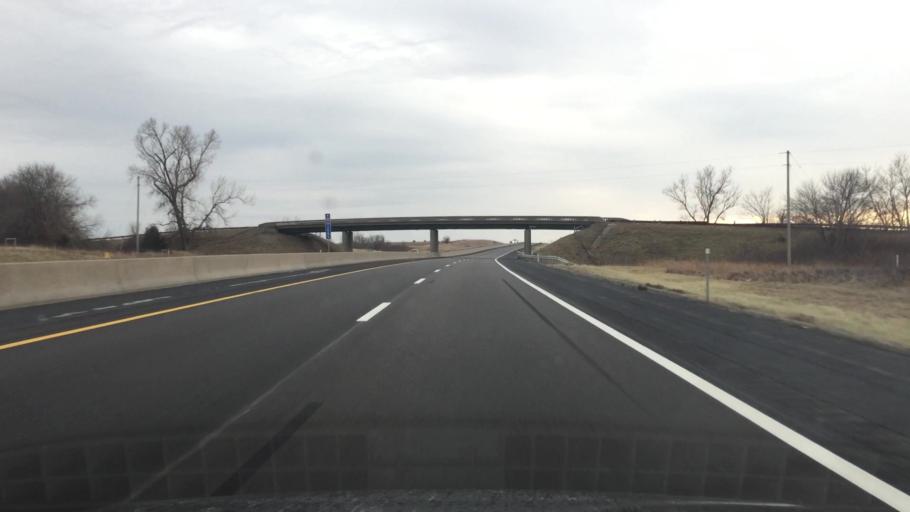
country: US
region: Kansas
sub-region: Osage County
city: Osage City
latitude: 38.7666
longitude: -95.9275
